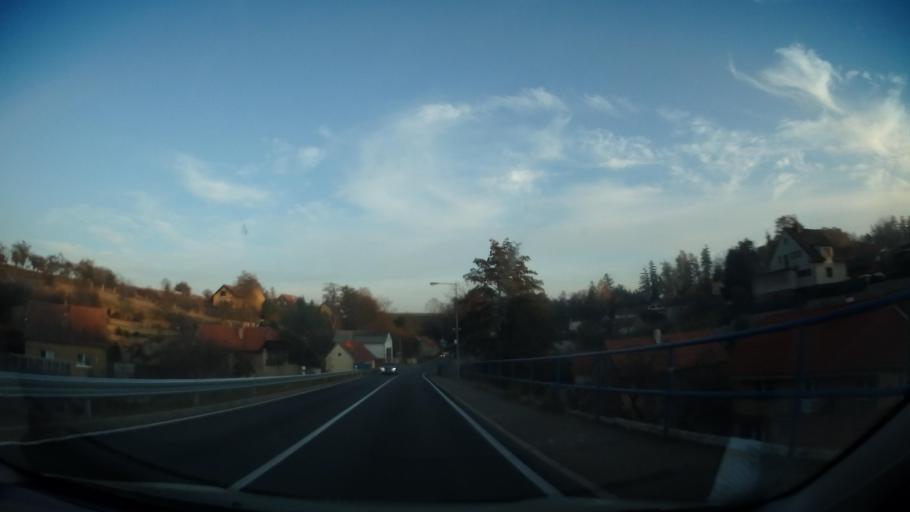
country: CZ
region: Central Bohemia
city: Vlasim
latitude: 49.7131
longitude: 14.8812
